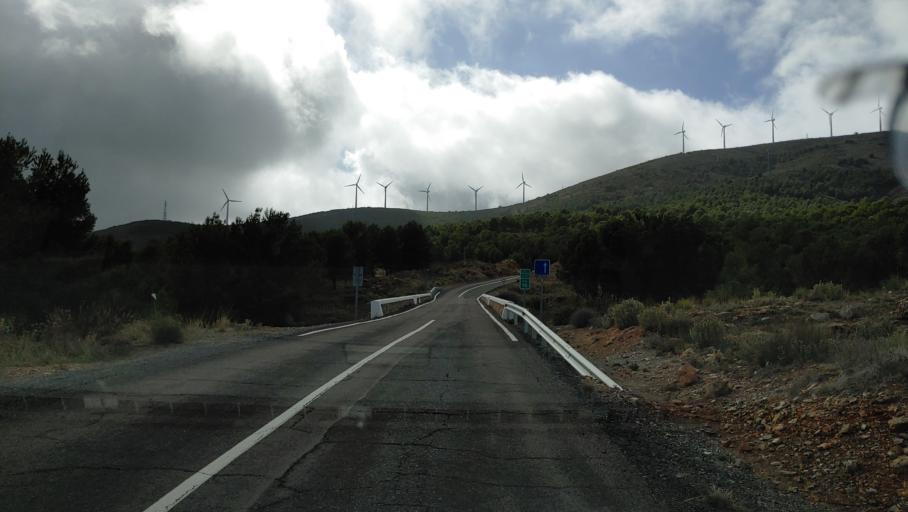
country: ES
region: Andalusia
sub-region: Provincia de Almeria
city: Enix
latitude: 36.9067
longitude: -2.6095
